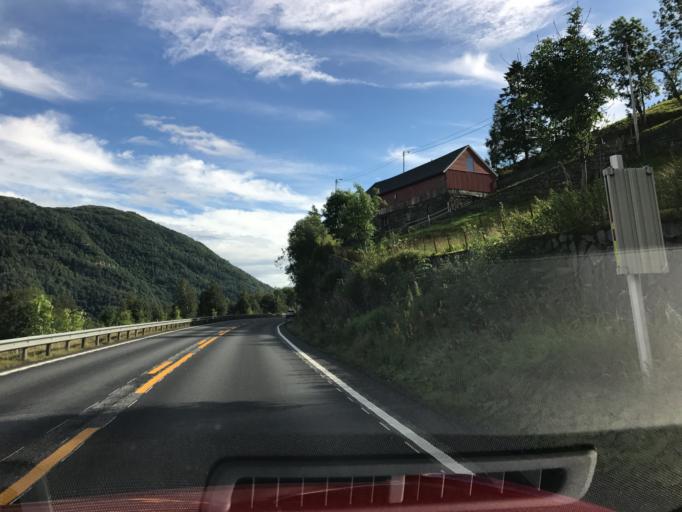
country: NO
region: Hordaland
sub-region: Bergen
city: Indre Arna
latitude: 60.4262
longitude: 5.5713
